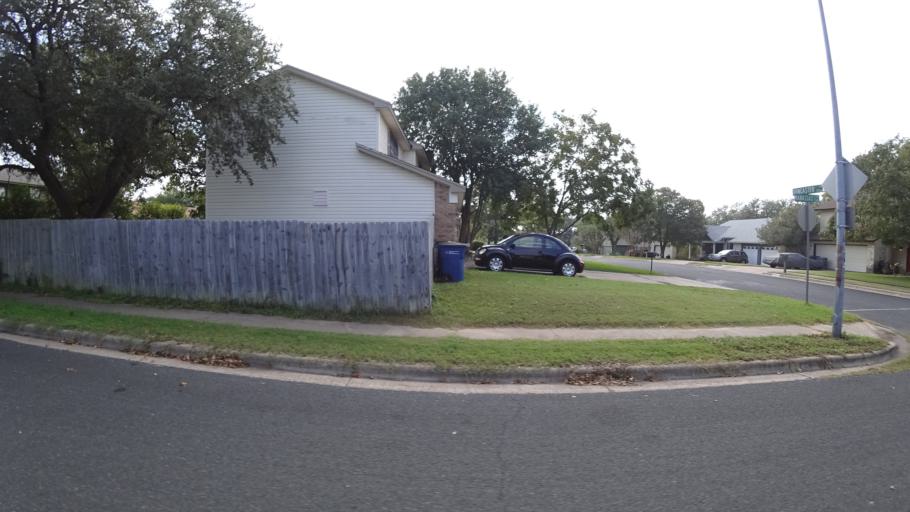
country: US
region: Texas
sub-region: Travis County
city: Shady Hollow
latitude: 30.1987
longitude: -97.8185
